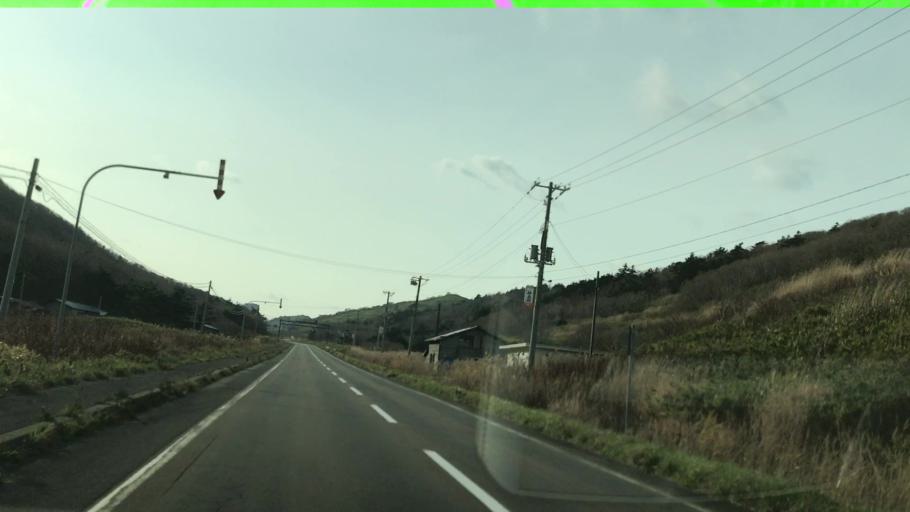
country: JP
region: Hokkaido
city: Iwanai
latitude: 43.3279
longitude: 140.3653
